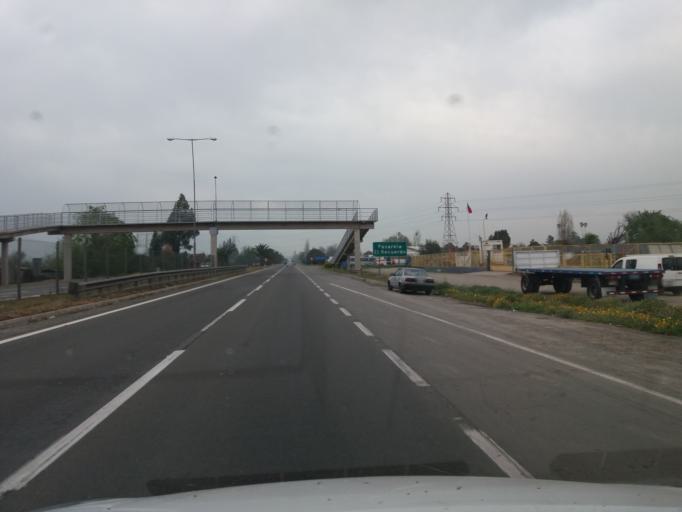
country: CL
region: Valparaiso
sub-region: Provincia de Quillota
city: Hacienda La Calera
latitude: -32.7738
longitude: -71.1859
